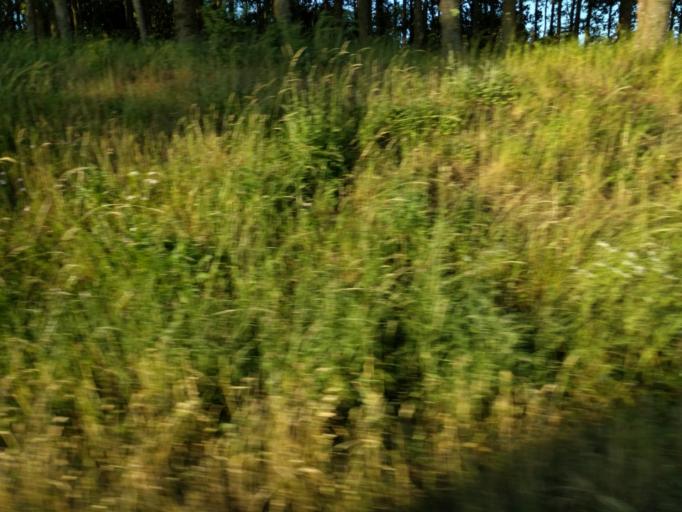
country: DK
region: South Denmark
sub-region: Kerteminde Kommune
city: Kerteminde
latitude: 55.5715
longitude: 10.6465
